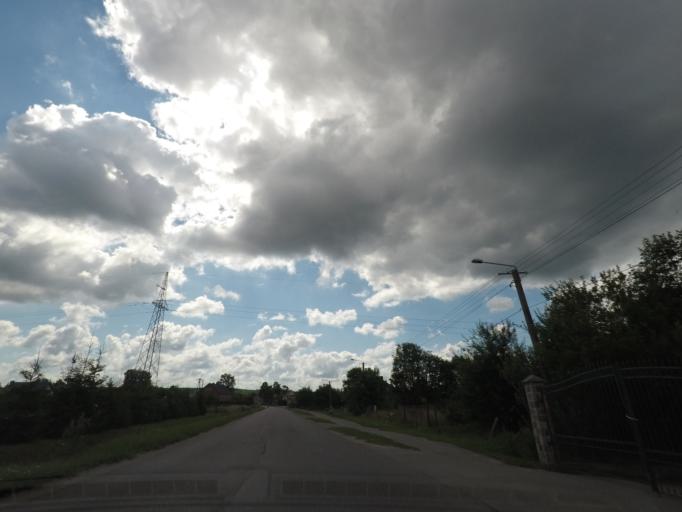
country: PL
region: Pomeranian Voivodeship
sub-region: Powiat wejherowski
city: Leczyce
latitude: 54.5869
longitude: 17.8613
